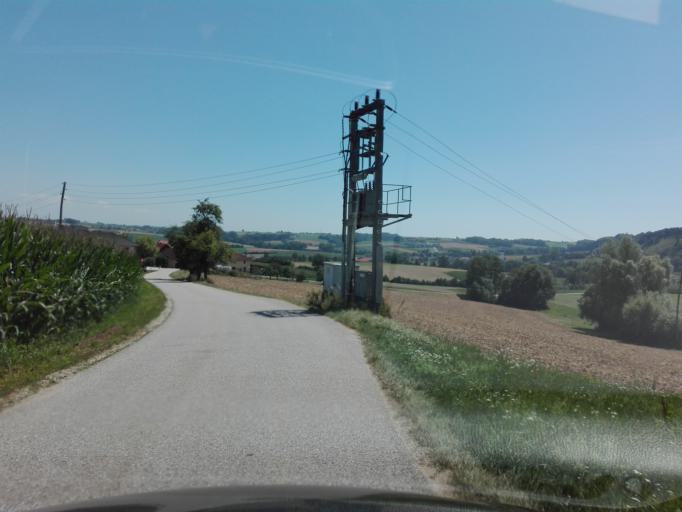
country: AT
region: Upper Austria
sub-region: Politischer Bezirk Urfahr-Umgebung
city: Engerwitzdorf
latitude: 48.2969
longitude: 14.4597
